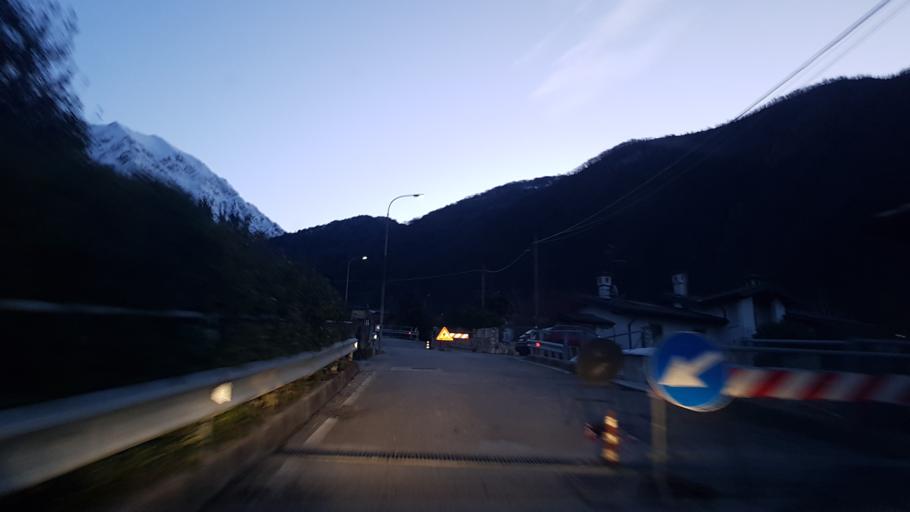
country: IT
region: Friuli Venezia Giulia
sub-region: Provincia di Udine
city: Gemona
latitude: 46.2811
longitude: 13.1426
